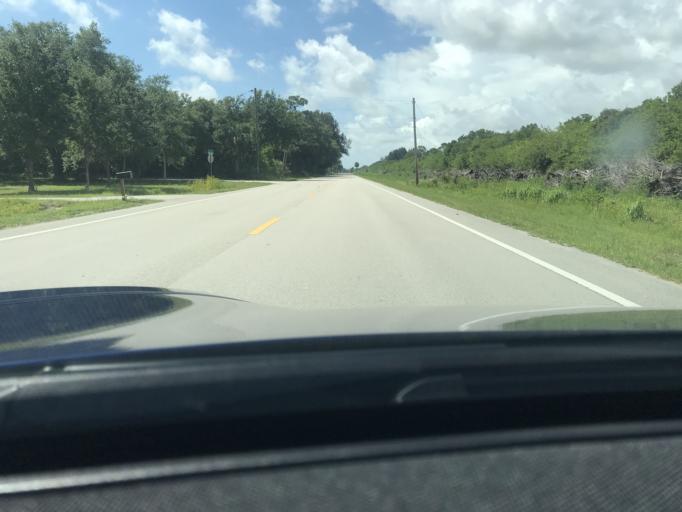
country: US
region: Florida
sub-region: Indian River County
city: Winter Beach
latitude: 27.7434
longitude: -80.4344
